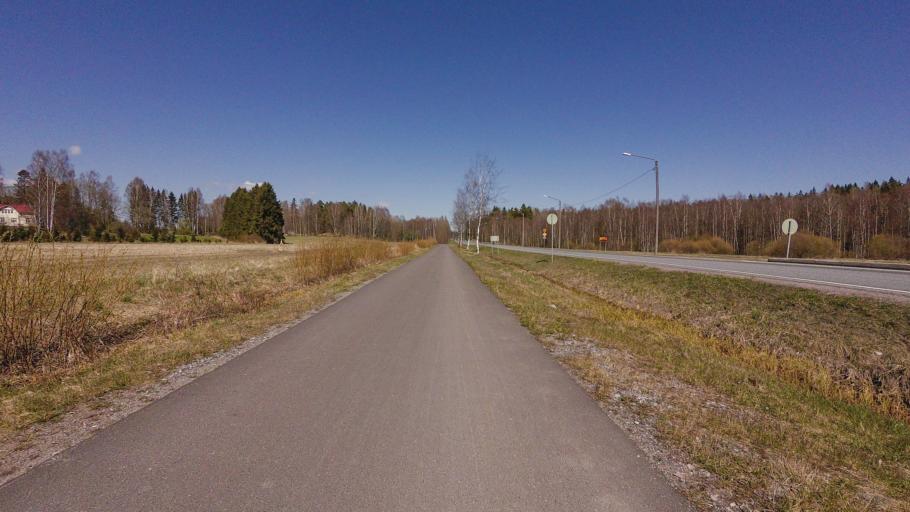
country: FI
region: Uusimaa
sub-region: Helsinki
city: Vantaa
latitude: 60.2343
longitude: 25.1342
